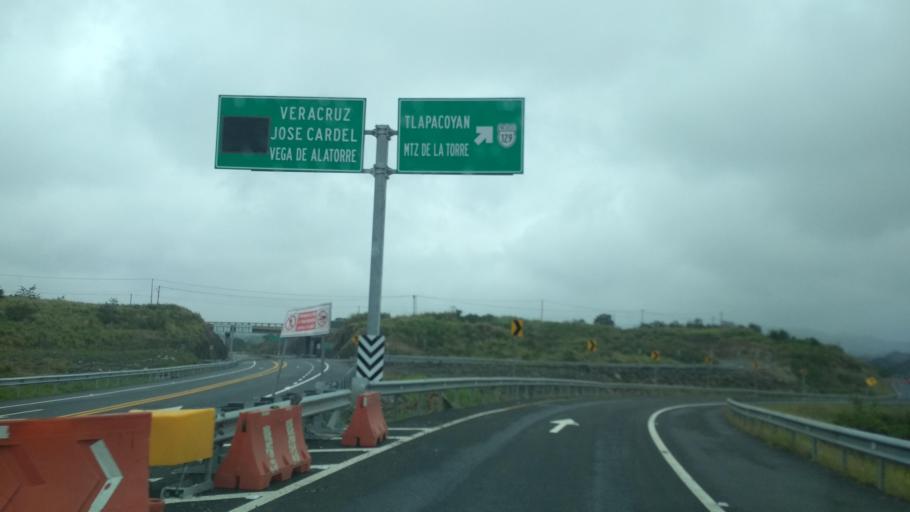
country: MX
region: Veracruz
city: Vega de San Marcos
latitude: 20.1492
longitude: -96.9480
